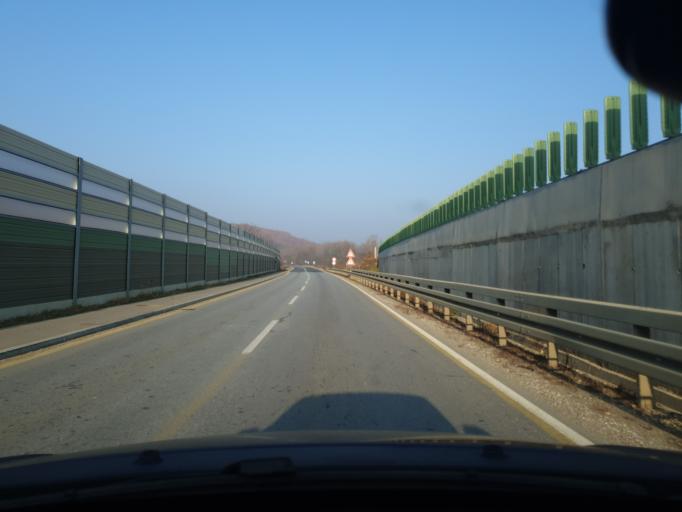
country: RS
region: Central Serbia
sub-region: Jablanicki Okrug
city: Vlasotince
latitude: 42.8931
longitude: 22.0569
